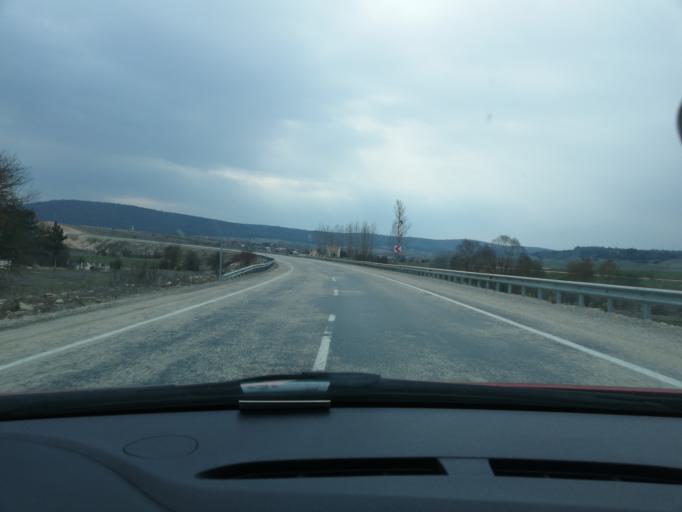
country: TR
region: Karabuk
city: Eflani
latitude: 41.4828
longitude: 33.0289
